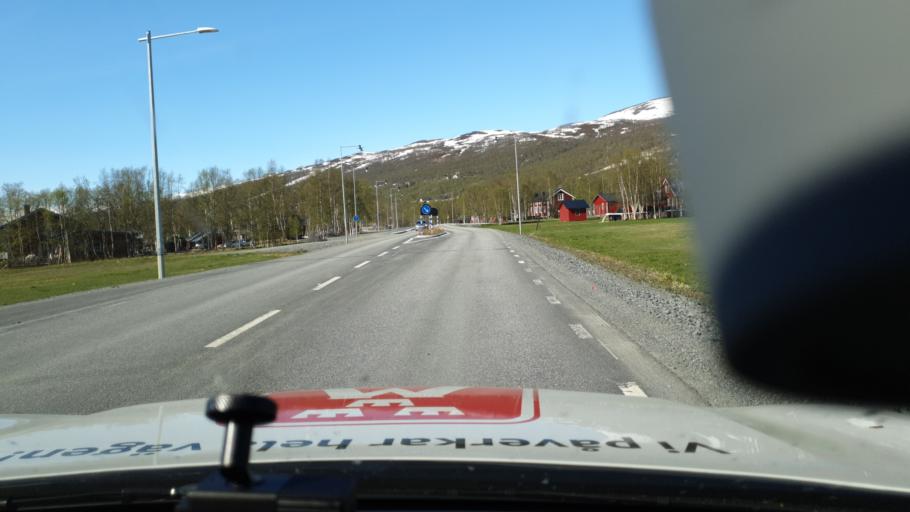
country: NO
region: Nordland
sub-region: Rana
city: Mo i Rana
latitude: 65.8088
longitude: 15.0883
